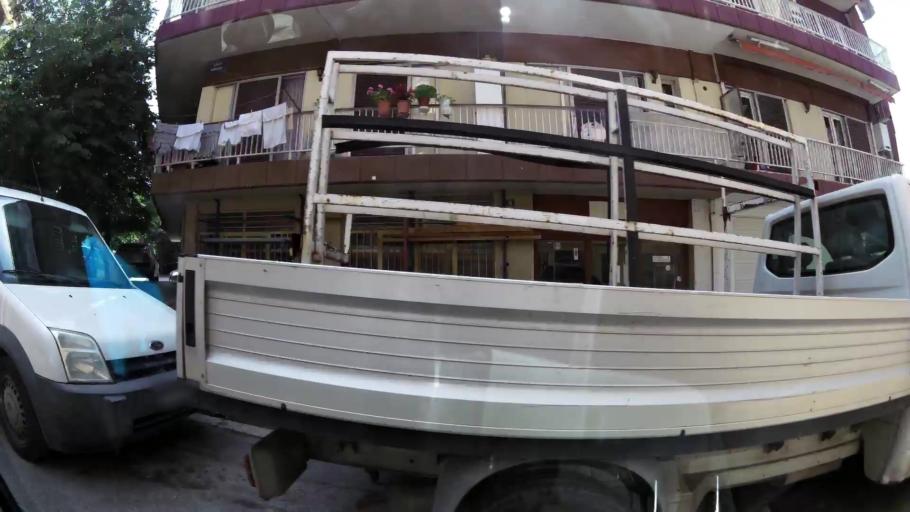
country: GR
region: Central Macedonia
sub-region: Nomos Thessalonikis
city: Triandria
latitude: 40.6170
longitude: 22.9724
